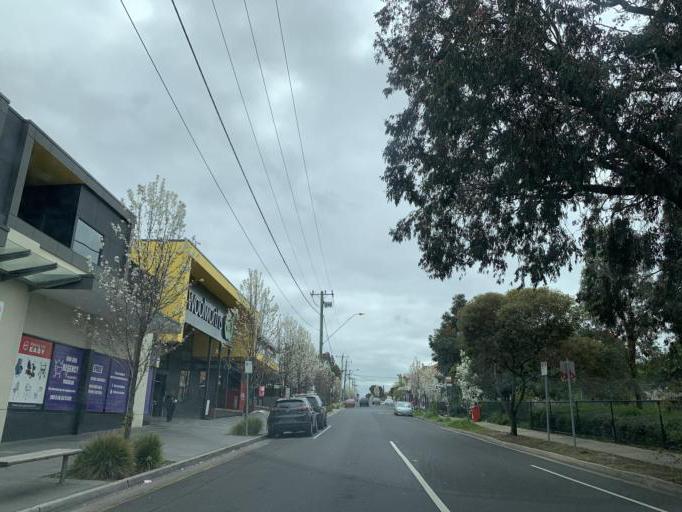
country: AU
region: Victoria
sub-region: Darebin
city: Reservoir
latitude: -37.7300
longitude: 144.9839
